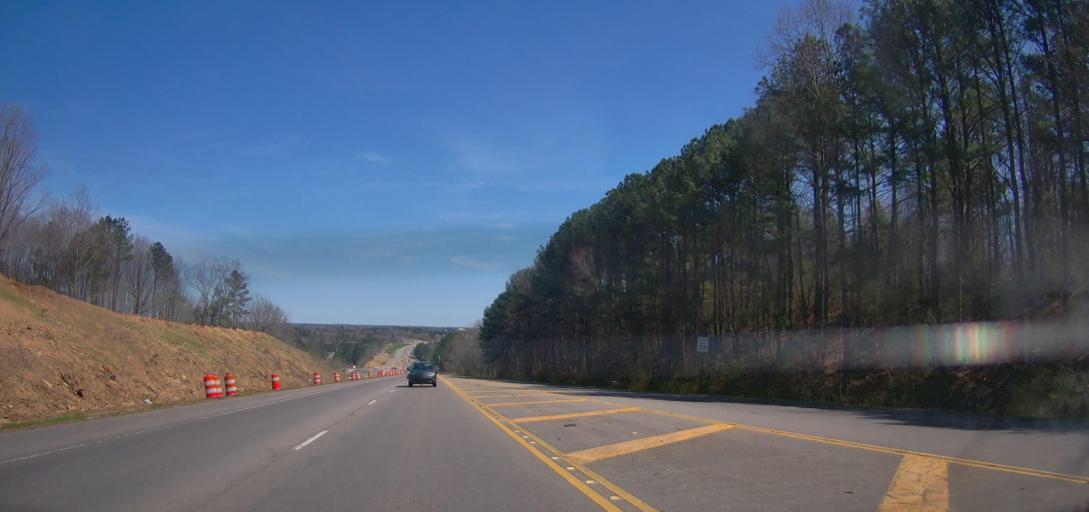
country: US
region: Alabama
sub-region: Cullman County
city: Cullman
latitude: 34.2063
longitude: -86.8539
